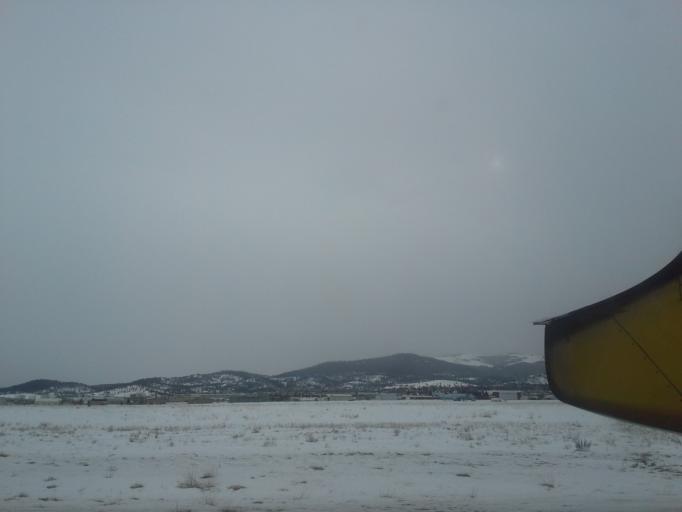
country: US
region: Montana
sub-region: Lewis and Clark County
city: Helena
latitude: 46.6085
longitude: -111.9865
